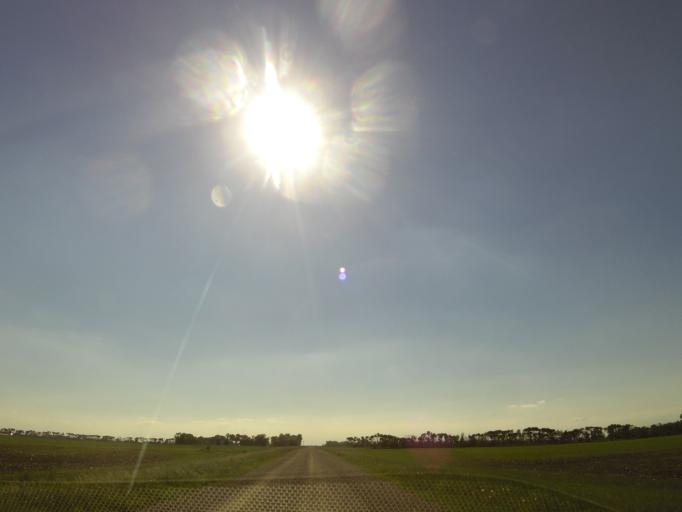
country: US
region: North Dakota
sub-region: Walsh County
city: Grafton
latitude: 48.3533
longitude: -97.2468
